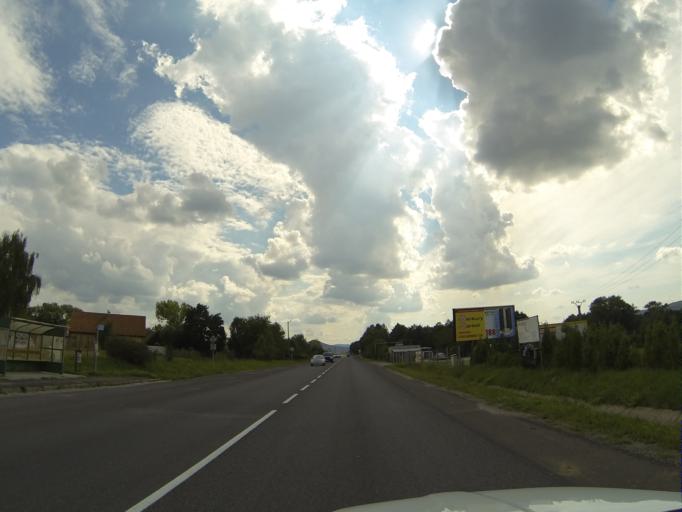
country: SK
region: Nitriansky
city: Novaky
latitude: 48.6618
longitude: 18.5113
